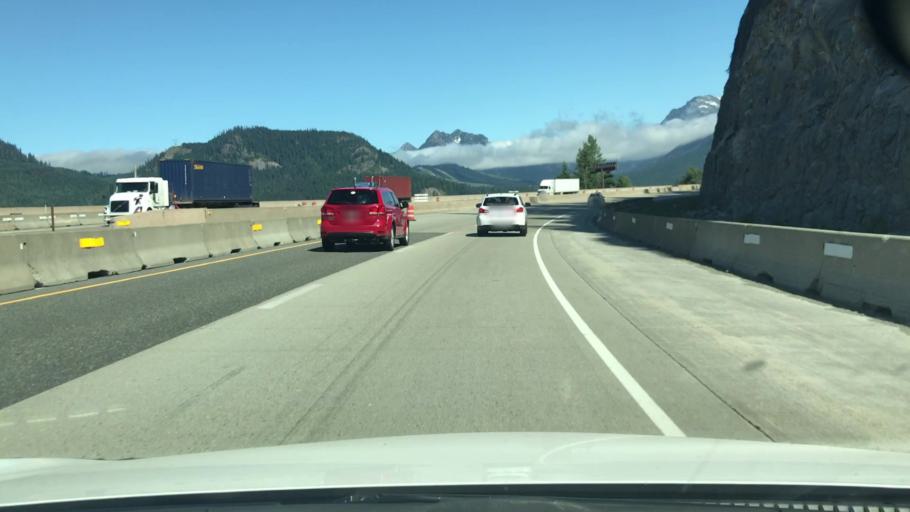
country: US
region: Washington
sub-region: King County
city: Tanner
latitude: 47.3609
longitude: -121.3719
